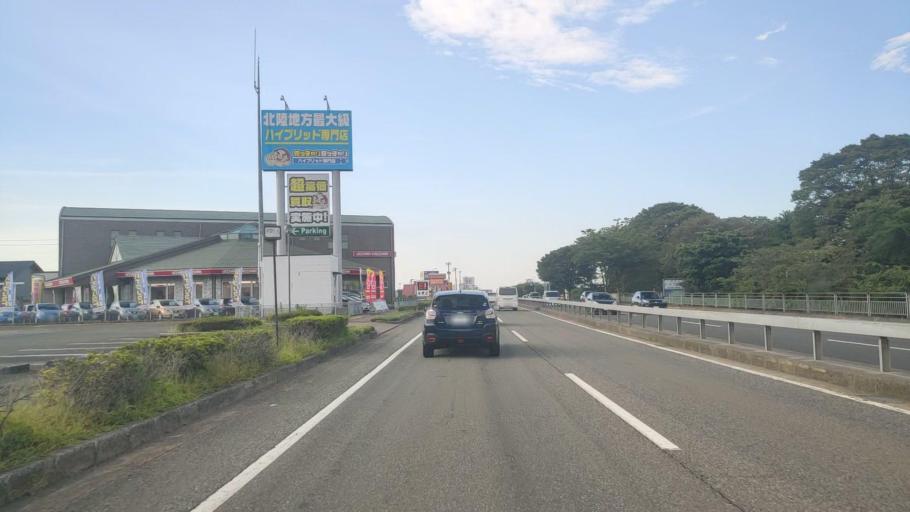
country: JP
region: Fukui
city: Sabae
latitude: 35.9621
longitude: 136.1884
